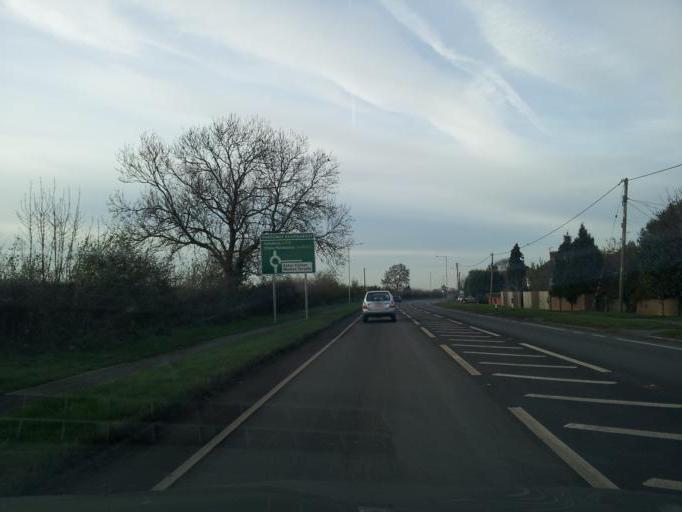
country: GB
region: England
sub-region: Buckinghamshire
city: Weston Turville
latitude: 51.7837
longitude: -0.7741
